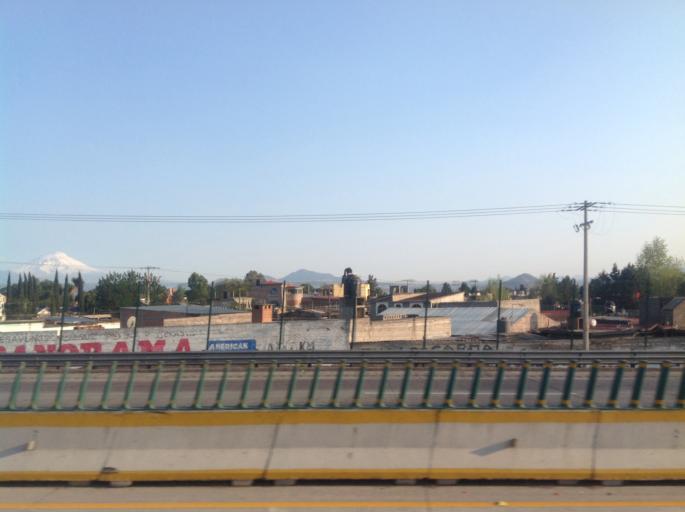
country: MX
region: Mexico
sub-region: Ixtapaluca
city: San Buenaventura
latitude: 19.2978
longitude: -98.8652
